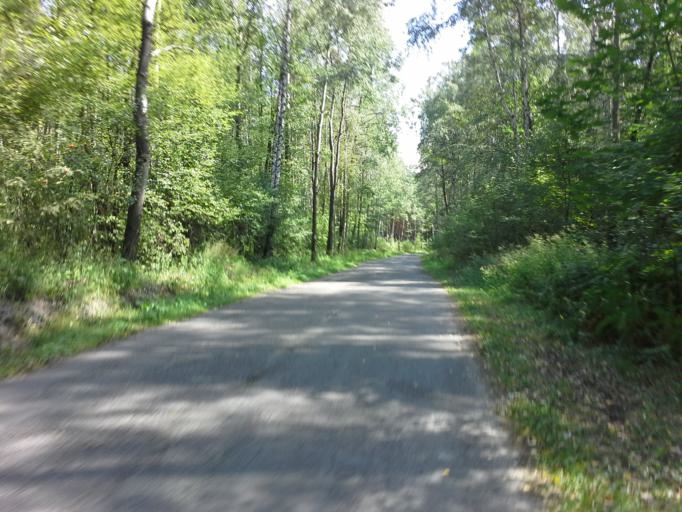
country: PL
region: Lesser Poland Voivodeship
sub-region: Powiat chrzanowski
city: Trzebinia
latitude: 50.1405
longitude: 19.4465
